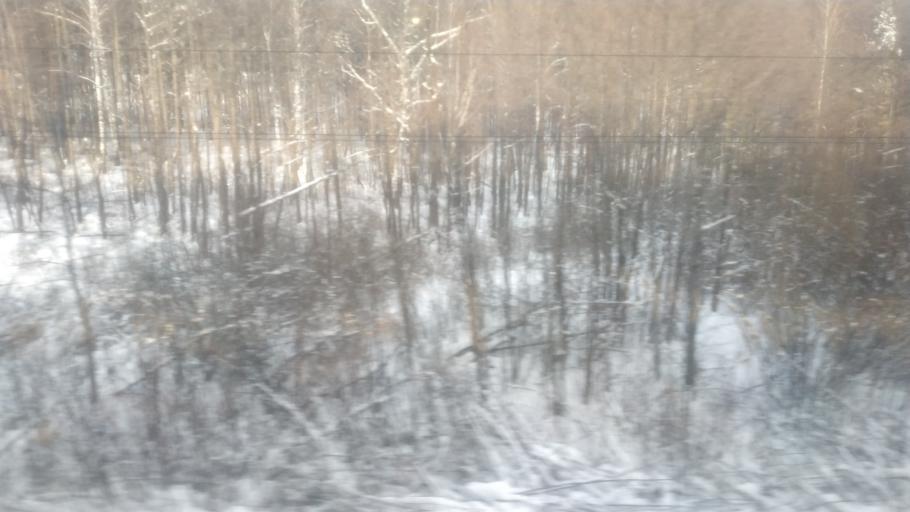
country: RU
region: Kirov
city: Krasnaya Polyana
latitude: 56.2506
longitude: 51.1487
